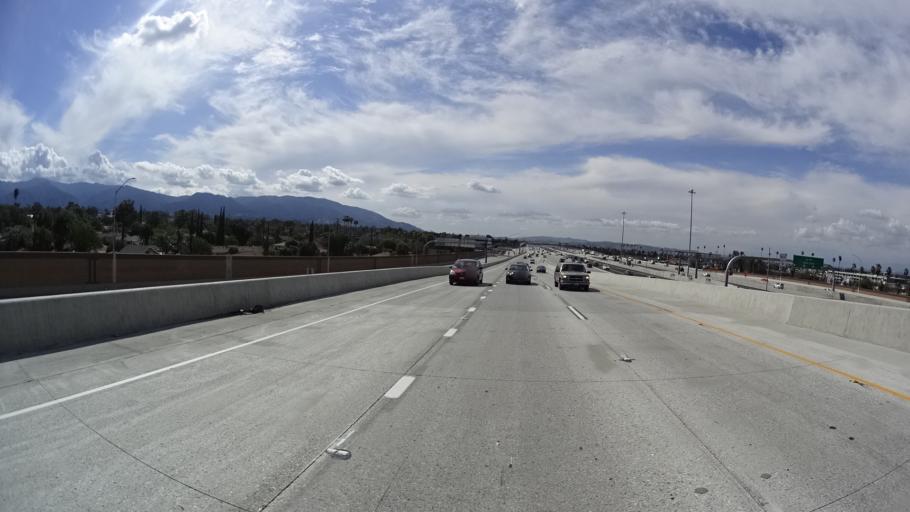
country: US
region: California
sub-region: Riverside County
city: Corona
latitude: 33.8795
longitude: -117.5613
